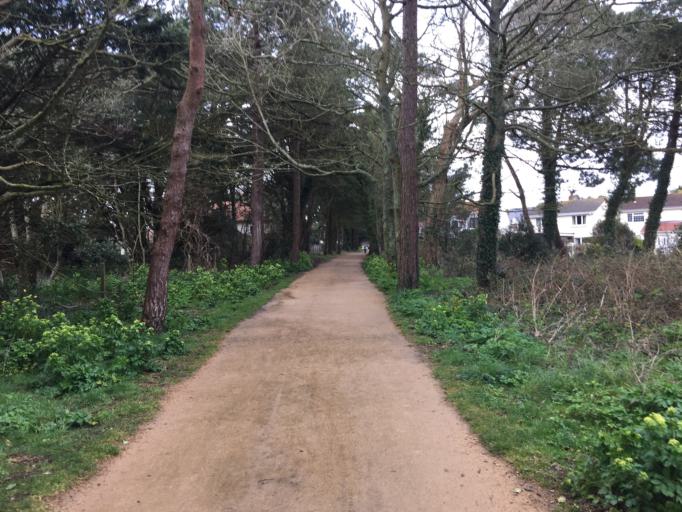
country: JE
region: St Helier
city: Saint Helier
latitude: 49.1881
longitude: -2.2185
